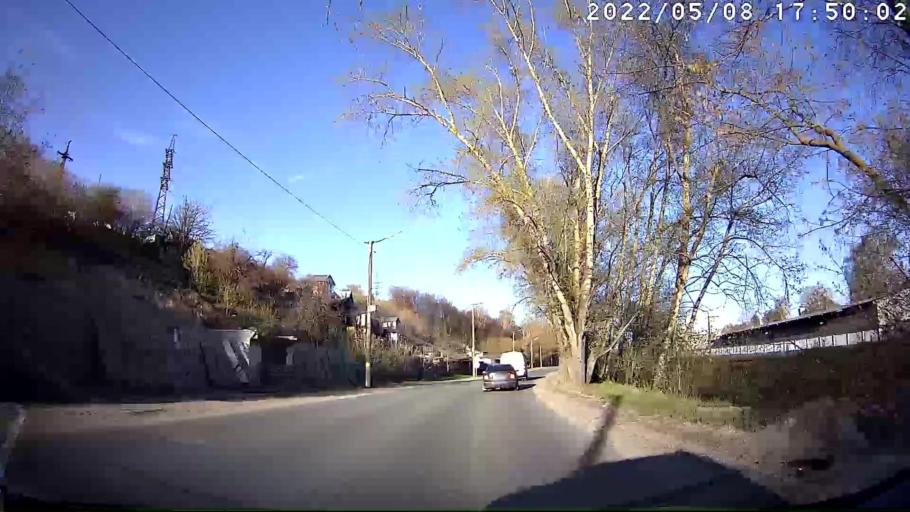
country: RU
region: Tatarstan
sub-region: Zelenodol'skiy Rayon
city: Zelenodolsk
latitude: 55.8434
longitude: 48.4840
